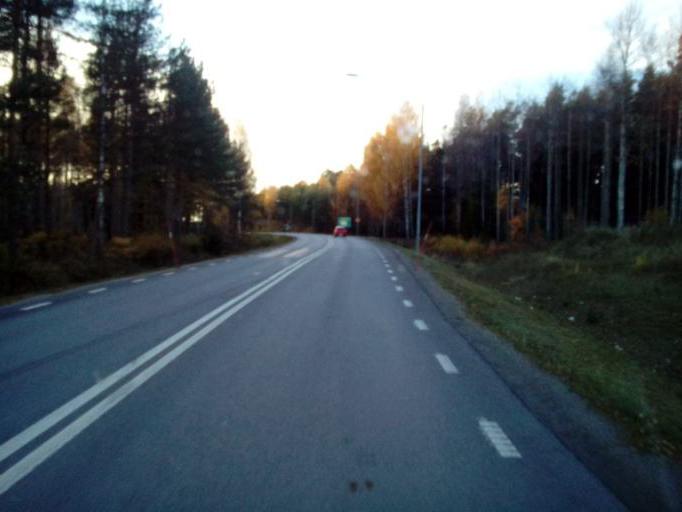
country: SE
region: OErebro
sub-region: Orebro Kommun
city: Orebro
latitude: 59.2147
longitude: 15.1512
